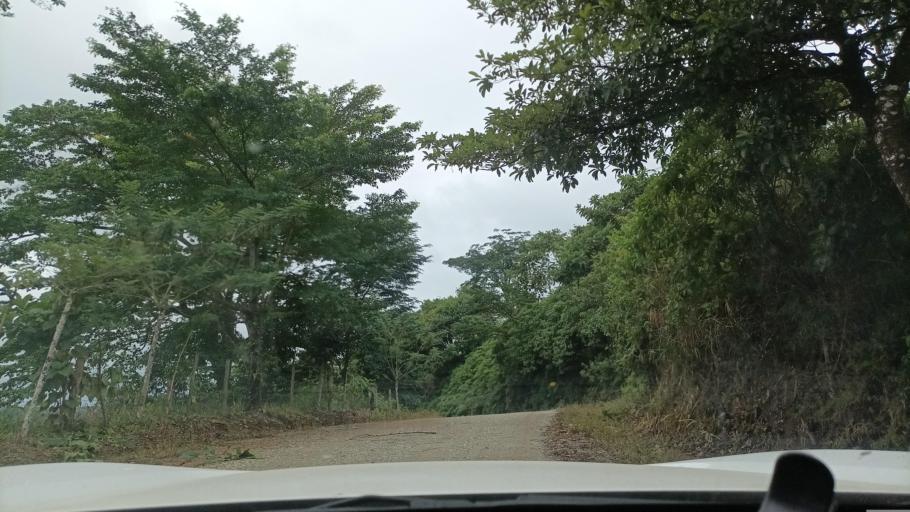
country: MX
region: Veracruz
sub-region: Uxpanapa
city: Poblado 10
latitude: 17.4346
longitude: -94.4157
